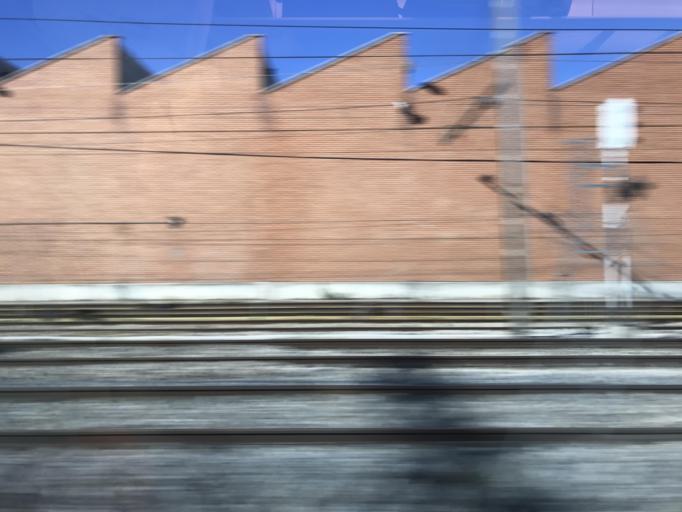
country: ES
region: Madrid
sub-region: Provincia de Madrid
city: Las Tablas
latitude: 40.5047
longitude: -3.6809
